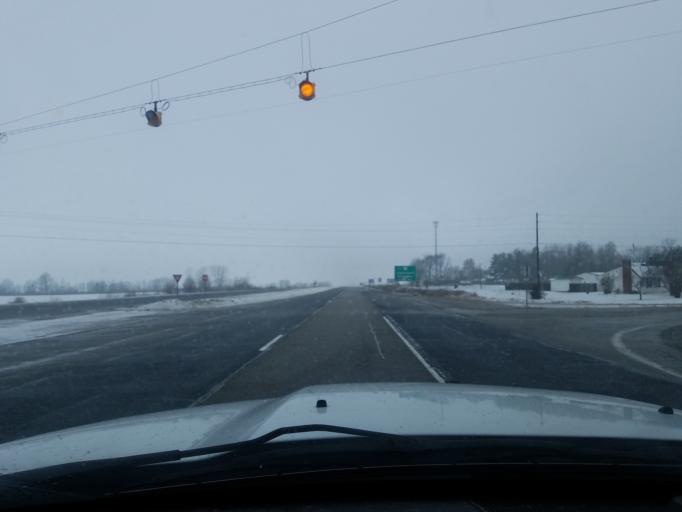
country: US
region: Indiana
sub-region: Fulton County
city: Rochester
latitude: 41.0420
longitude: -86.2021
